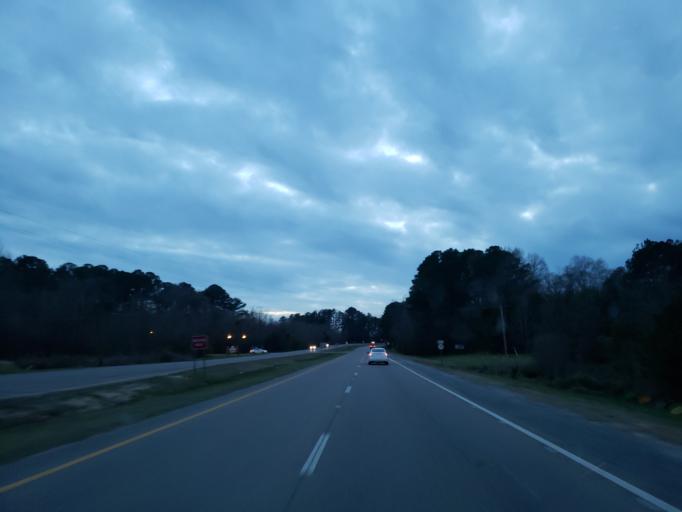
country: US
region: Mississippi
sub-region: Lauderdale County
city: Meridian
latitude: 32.3653
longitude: -88.6571
